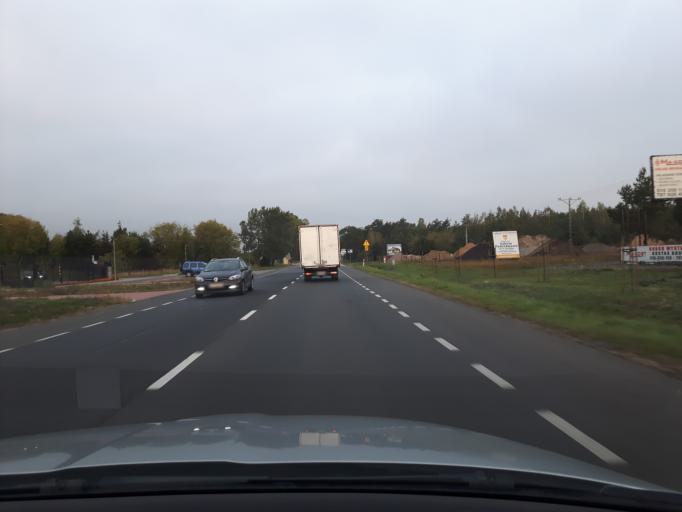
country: PL
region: Masovian Voivodeship
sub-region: Powiat warszawski zachodni
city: Dziekanow Lesny
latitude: 52.4069
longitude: 20.7966
